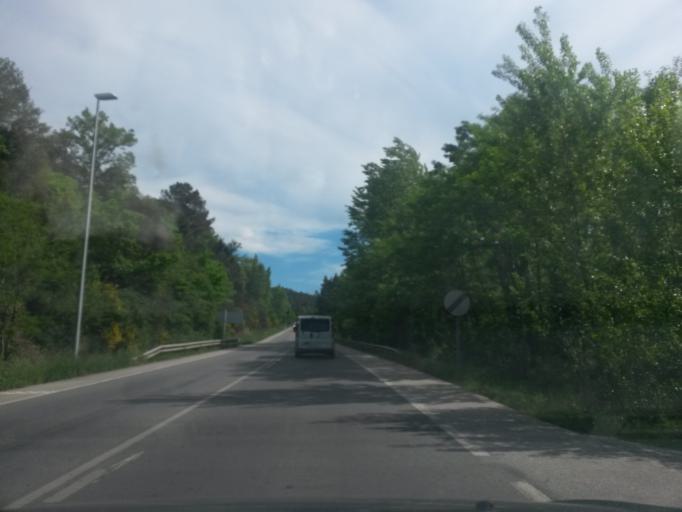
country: ES
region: Catalonia
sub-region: Provincia de Girona
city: Angles
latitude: 41.9492
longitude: 2.6408
